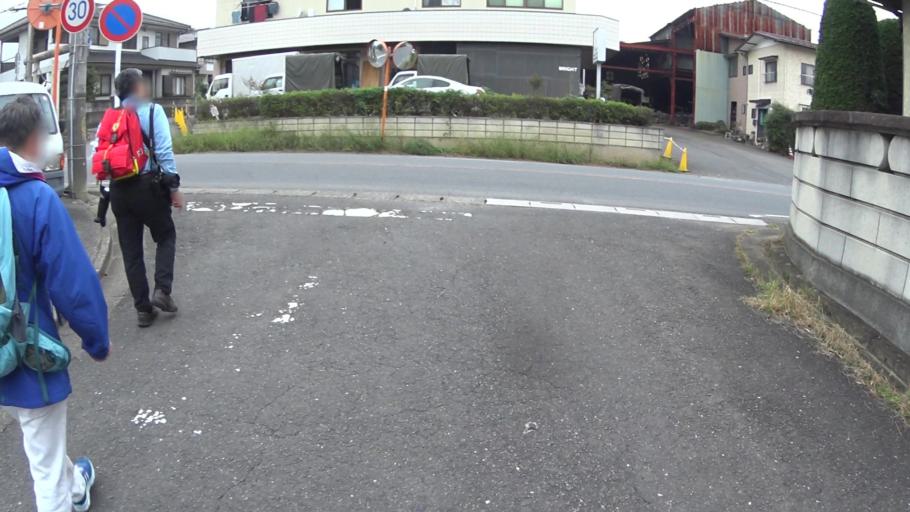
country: JP
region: Saitama
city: Hanno
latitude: 35.8623
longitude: 139.3247
